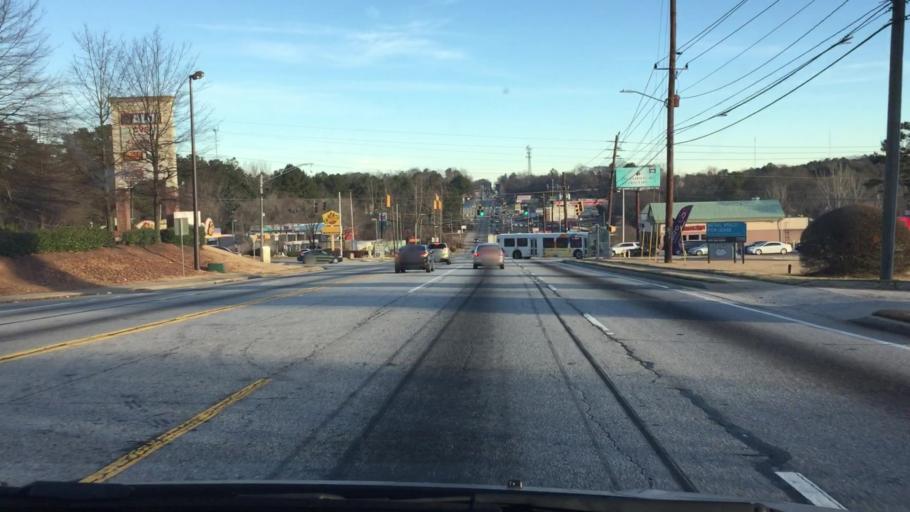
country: US
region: Georgia
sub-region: DeKalb County
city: Gresham Park
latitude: 33.7146
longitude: -84.3495
